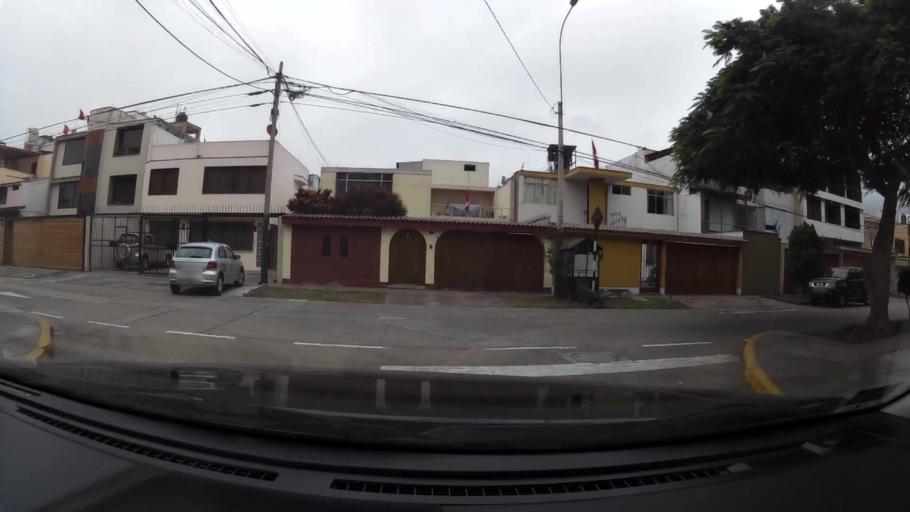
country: PE
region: Lima
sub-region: Lima
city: Surco
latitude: -12.1414
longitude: -76.9982
